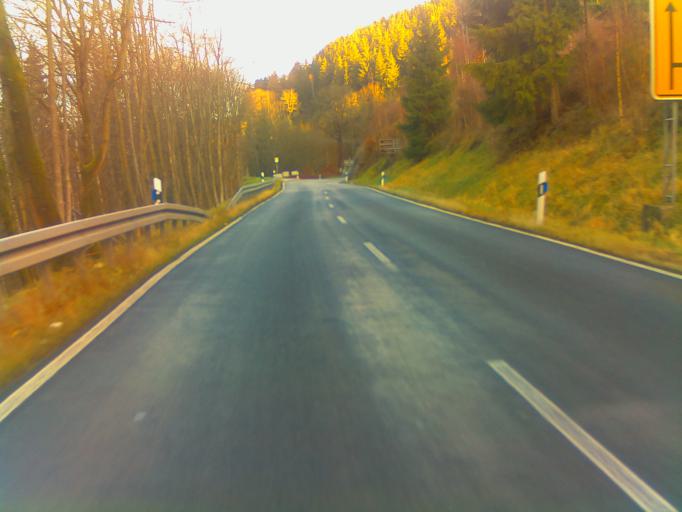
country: DE
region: Thuringia
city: Meuselbach
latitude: 50.5716
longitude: 11.0721
